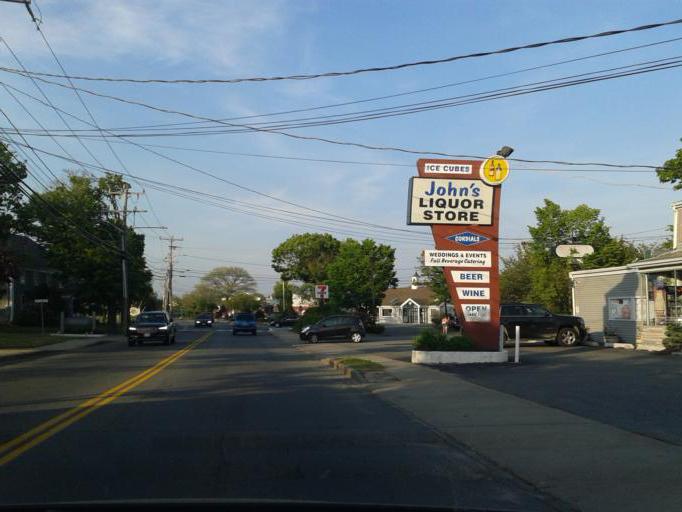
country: US
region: Massachusetts
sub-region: Barnstable County
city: Falmouth
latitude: 41.5532
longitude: -70.6035
